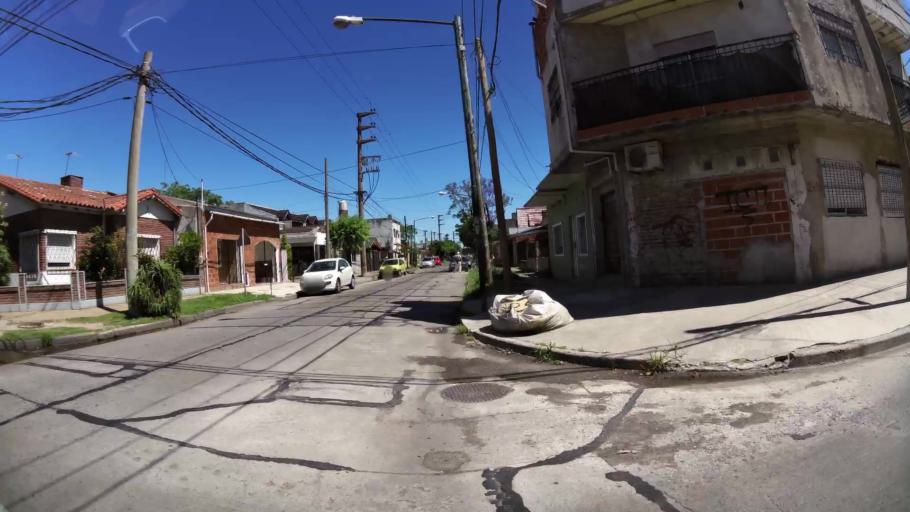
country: AR
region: Buenos Aires
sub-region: Partido de General San Martin
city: General San Martin
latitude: -34.5277
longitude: -58.5528
